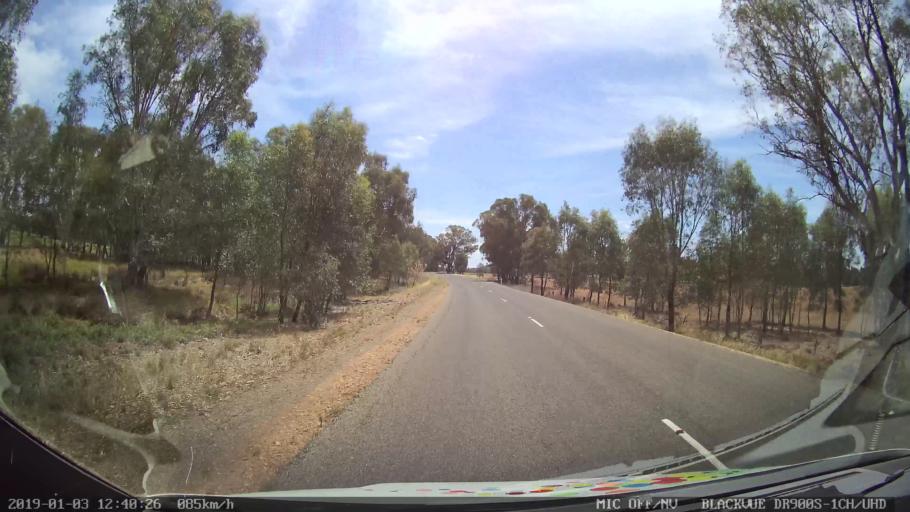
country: AU
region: New South Wales
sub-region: Weddin
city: Grenfell
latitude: -33.8126
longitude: 148.2122
